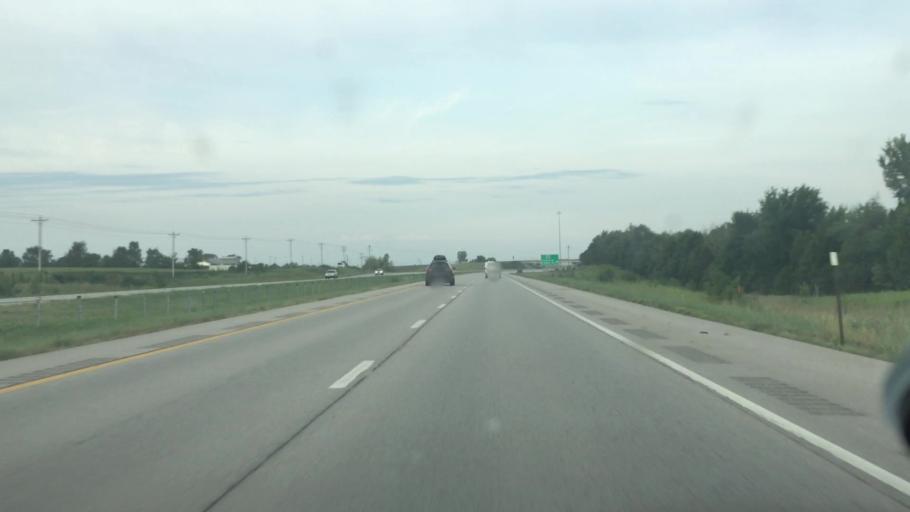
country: US
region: Kansas
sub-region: Douglas County
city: Eudora
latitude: 38.9332
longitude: -95.0872
